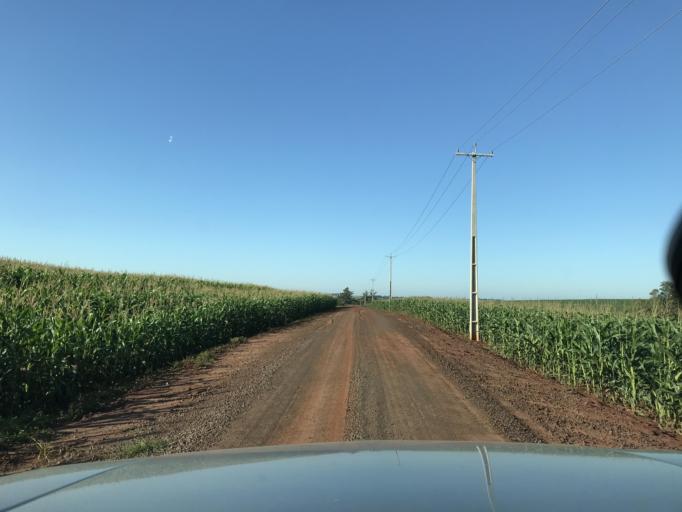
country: BR
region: Parana
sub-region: Palotina
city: Palotina
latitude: -24.2160
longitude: -53.7487
